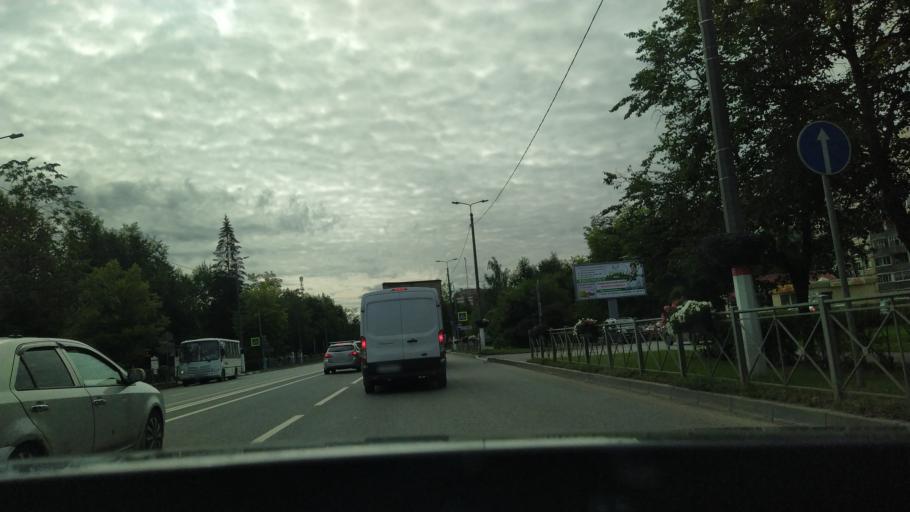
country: RU
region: Leningrad
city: Tosno
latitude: 59.5440
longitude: 30.8714
